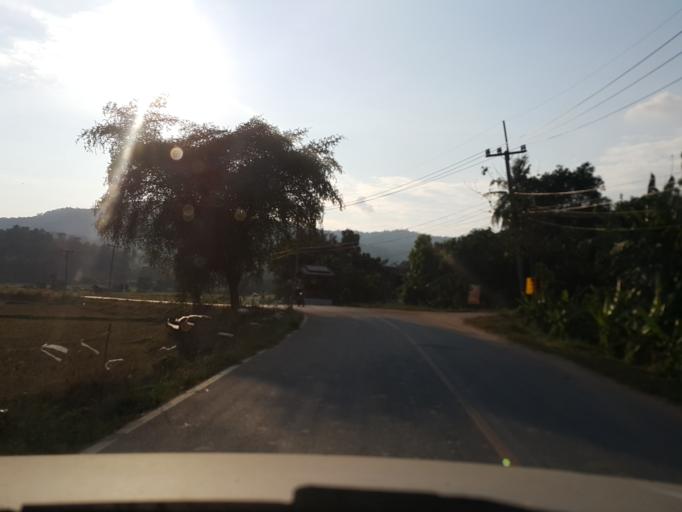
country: TH
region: Chiang Mai
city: Mae On
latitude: 18.6284
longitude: 99.2829
